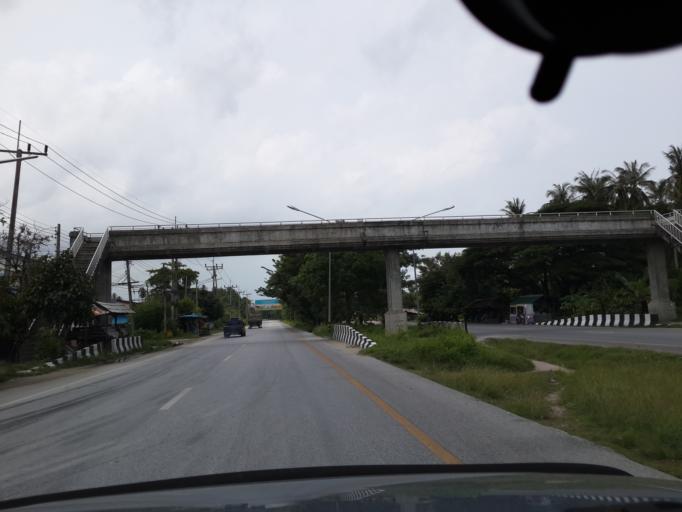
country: TH
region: Pattani
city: Yaring
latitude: 6.8698
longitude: 101.3209
